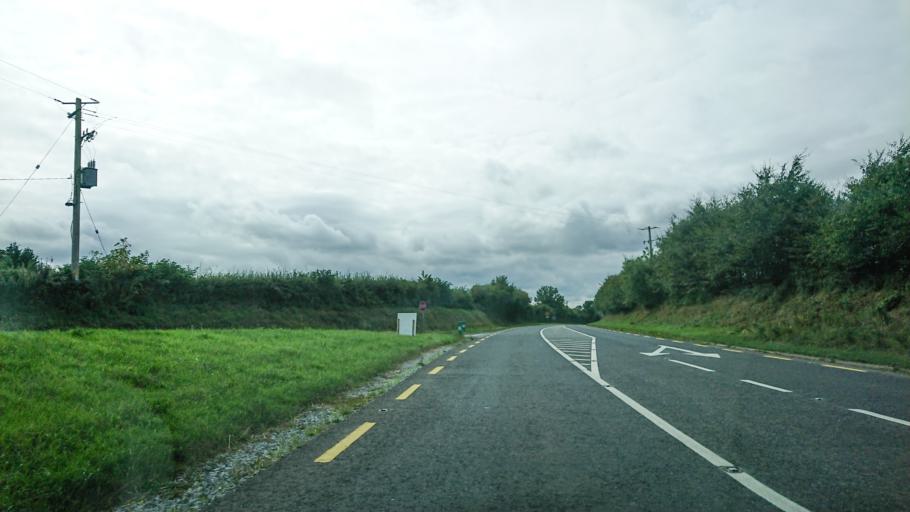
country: IE
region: Munster
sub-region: County Cork
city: Mallow
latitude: 52.1554
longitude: -8.5045
